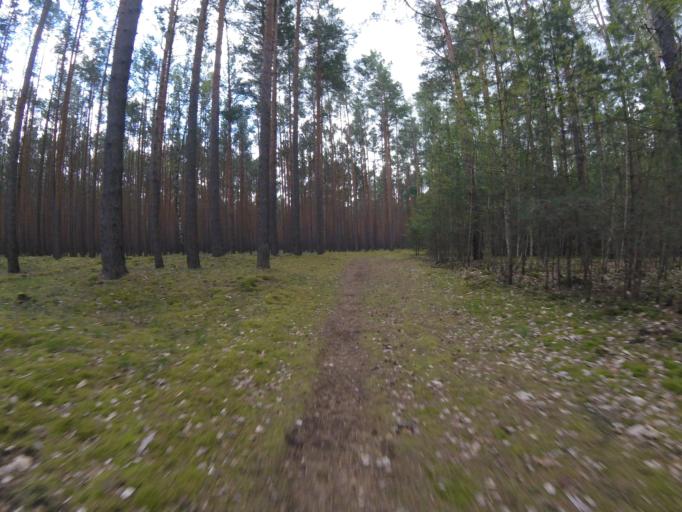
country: DE
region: Brandenburg
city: Bestensee
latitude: 52.2621
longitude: 13.6734
